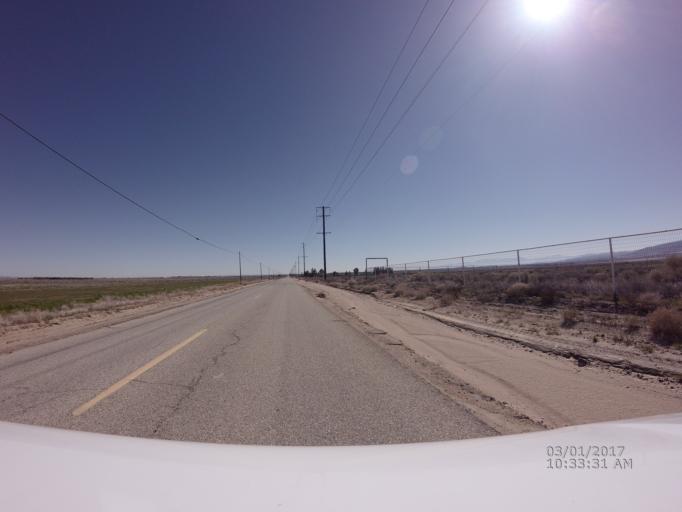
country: US
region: California
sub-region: Los Angeles County
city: Leona Valley
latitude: 34.6893
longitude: -118.2793
